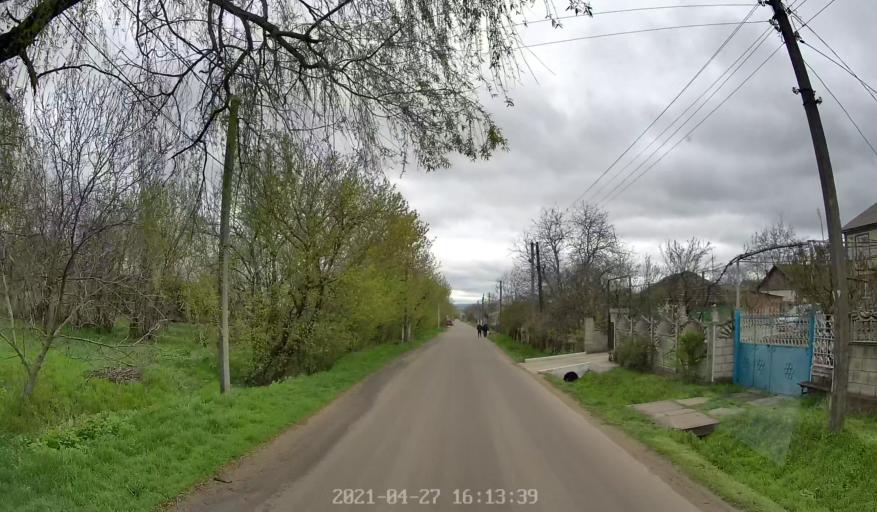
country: MD
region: Chisinau
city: Singera
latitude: 47.0076
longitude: 29.0132
